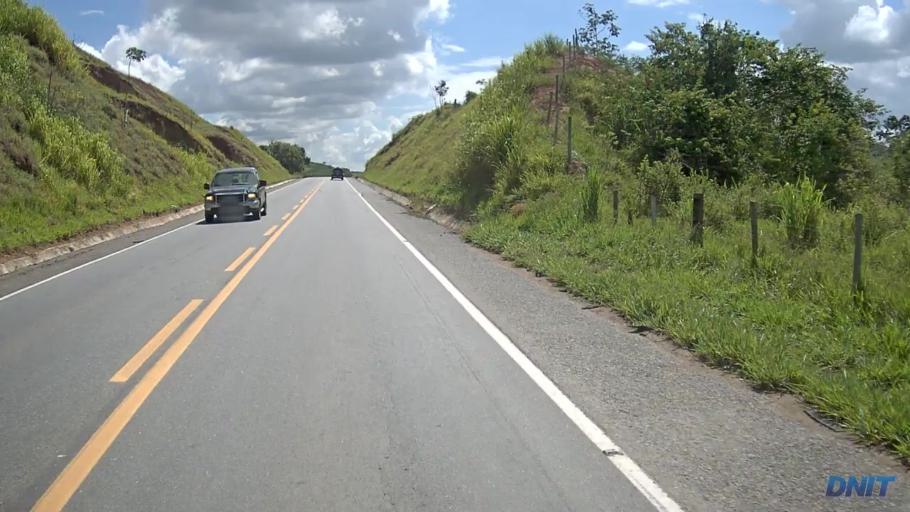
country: BR
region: Minas Gerais
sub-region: Governador Valadares
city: Governador Valadares
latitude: -18.9972
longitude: -42.1217
